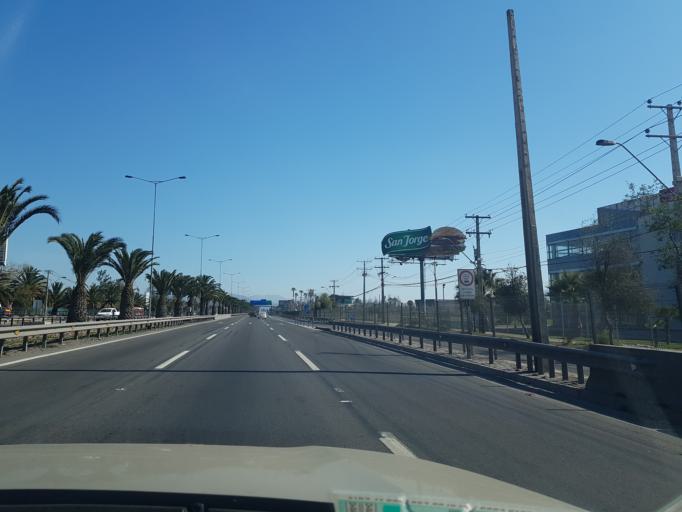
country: CL
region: Santiago Metropolitan
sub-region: Provincia de Santiago
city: Lo Prado
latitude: -33.3884
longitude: -70.7625
